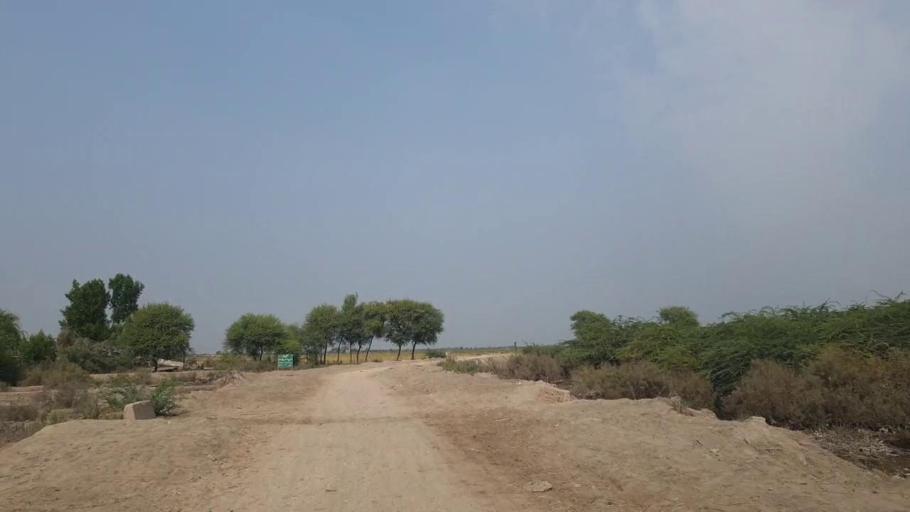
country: PK
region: Sindh
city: Badin
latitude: 24.6178
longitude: 68.7411
